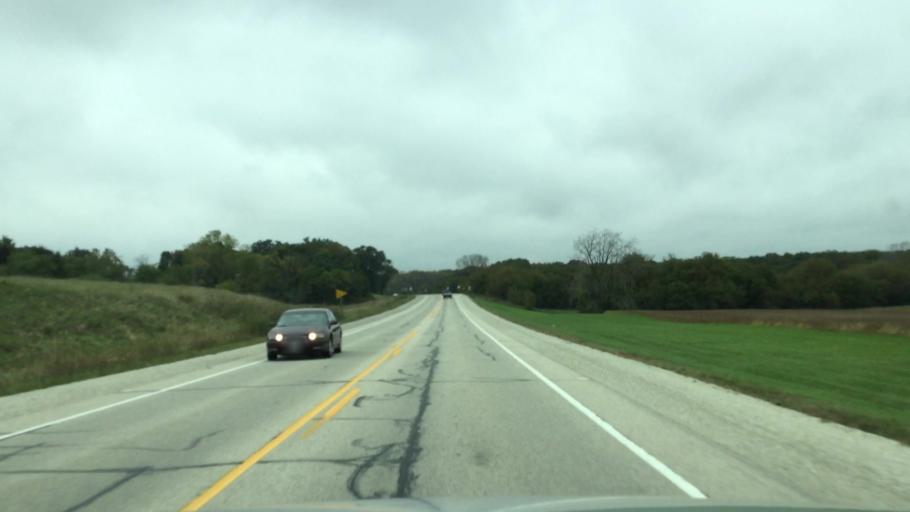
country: US
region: Wisconsin
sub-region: Racine County
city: Eagle Lake
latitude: 42.7422
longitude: -88.1414
